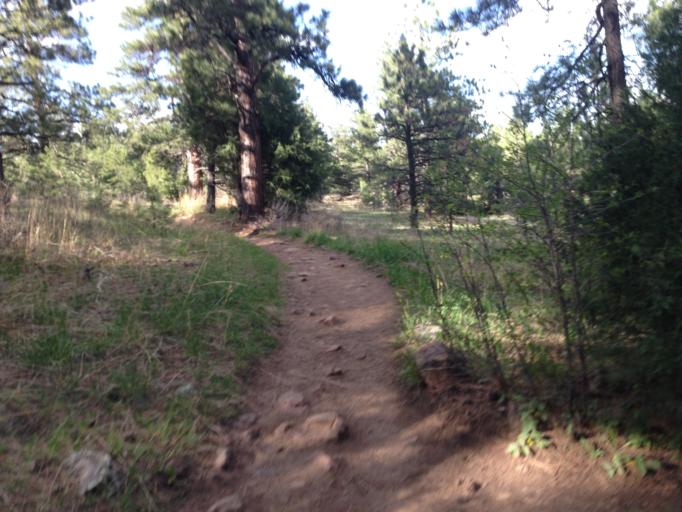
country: US
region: Colorado
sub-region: Boulder County
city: Boulder
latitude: 39.9475
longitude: -105.2794
